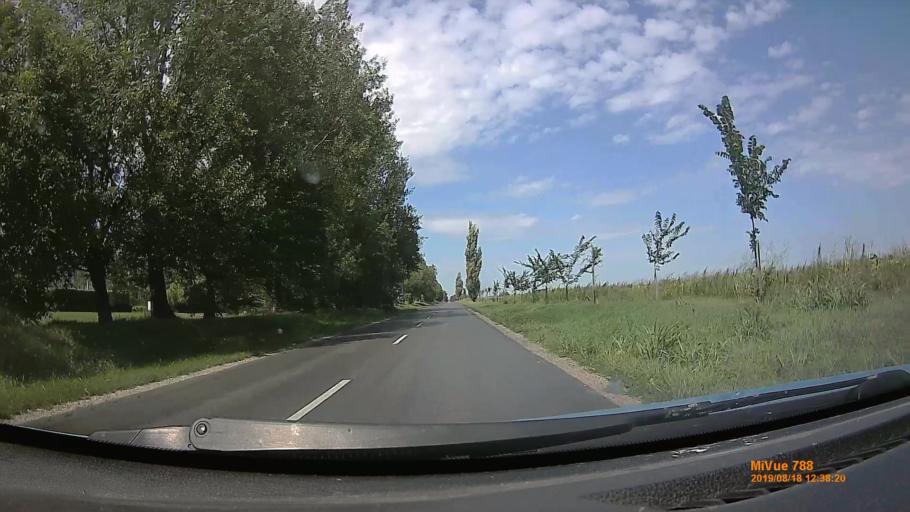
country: HU
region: Fejer
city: Szabadbattyan
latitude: 47.0879
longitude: 18.3998
